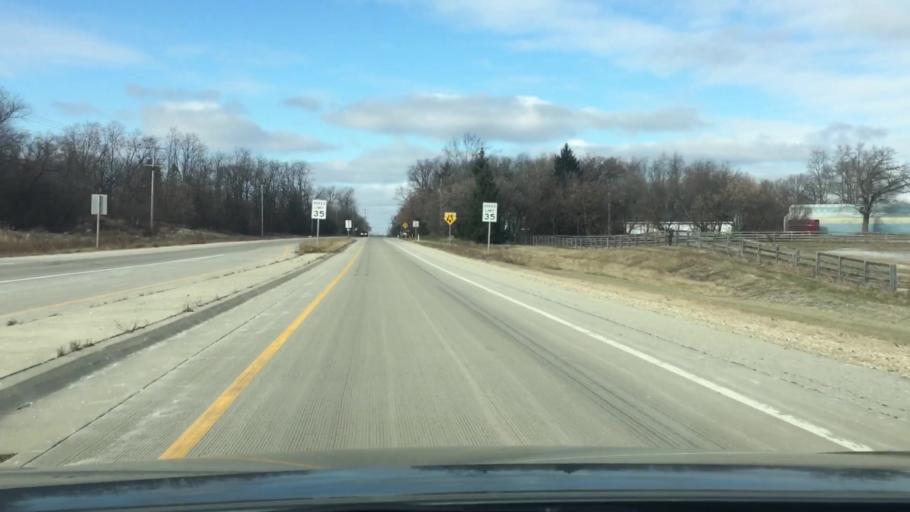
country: US
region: Wisconsin
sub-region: Waukesha County
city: North Prairie
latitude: 42.9497
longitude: -88.3538
